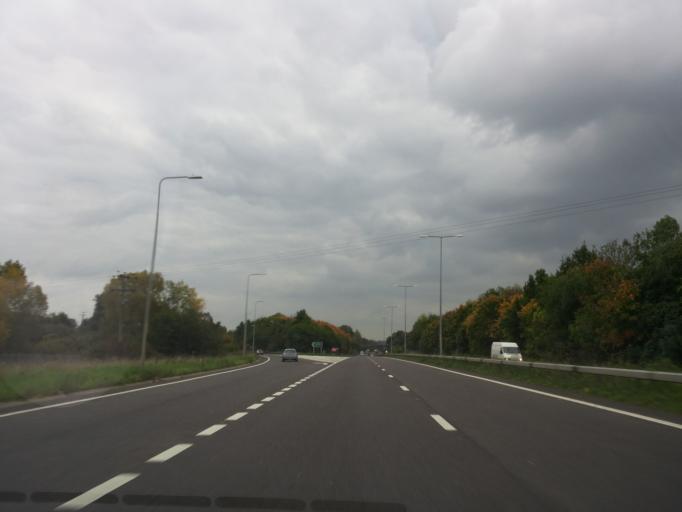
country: GB
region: England
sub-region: Kent
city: Blean
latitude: 51.2830
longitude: 1.0326
